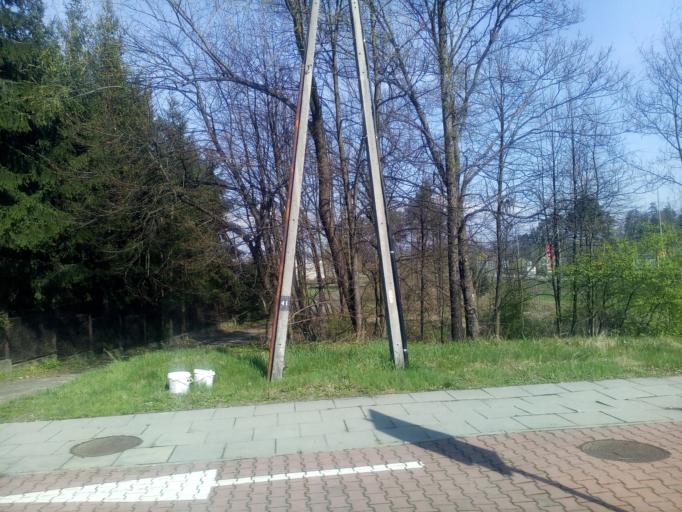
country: PL
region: Lesser Poland Voivodeship
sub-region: Powiat nowosadecki
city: Stary Sacz
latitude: 49.5670
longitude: 20.6562
